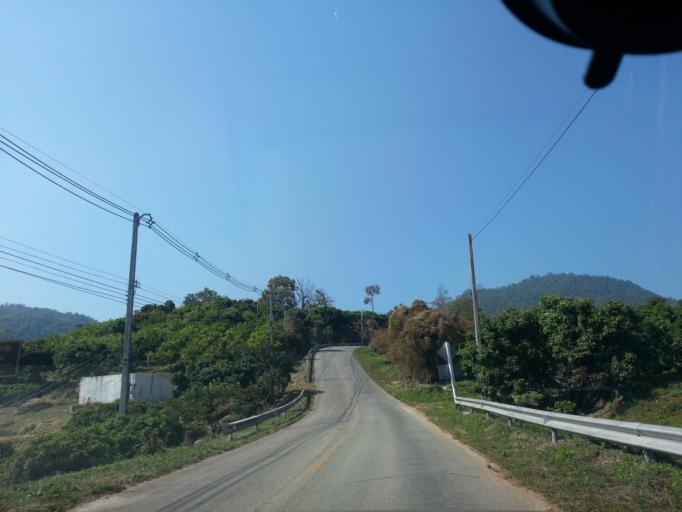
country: TH
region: Chiang Mai
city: Chai Prakan
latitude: 19.8298
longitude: 99.1018
